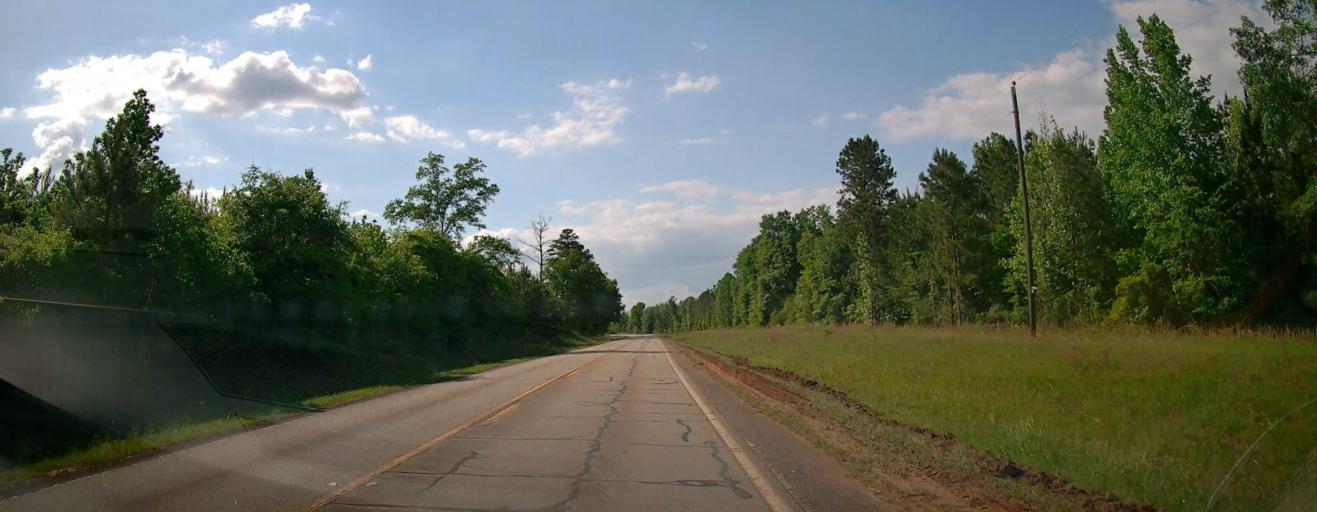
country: US
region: Georgia
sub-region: Washington County
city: Tennille
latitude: 32.9130
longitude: -82.9868
